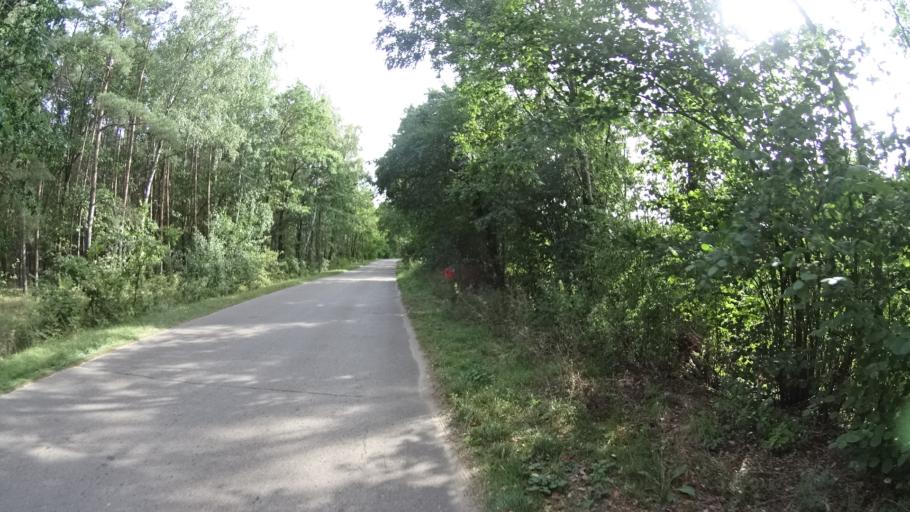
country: PL
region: Masovian Voivodeship
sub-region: Powiat legionowski
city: Serock
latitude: 52.4935
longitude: 21.0860
